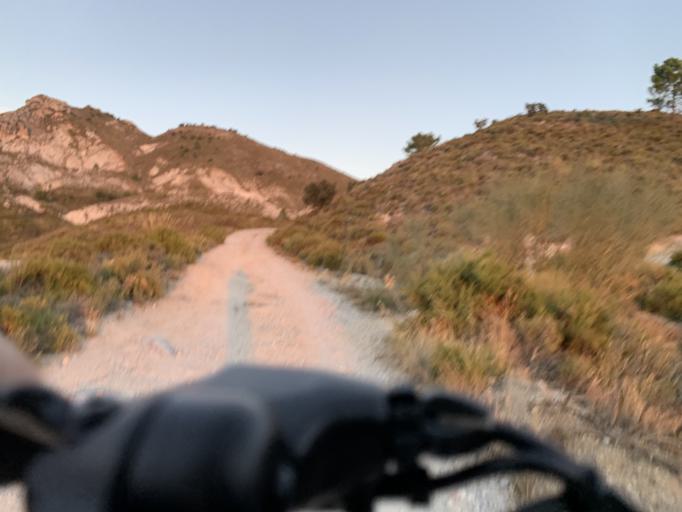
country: ES
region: Andalusia
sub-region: Provincia de Granada
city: Beas de Granada
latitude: 37.2265
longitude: -3.4640
